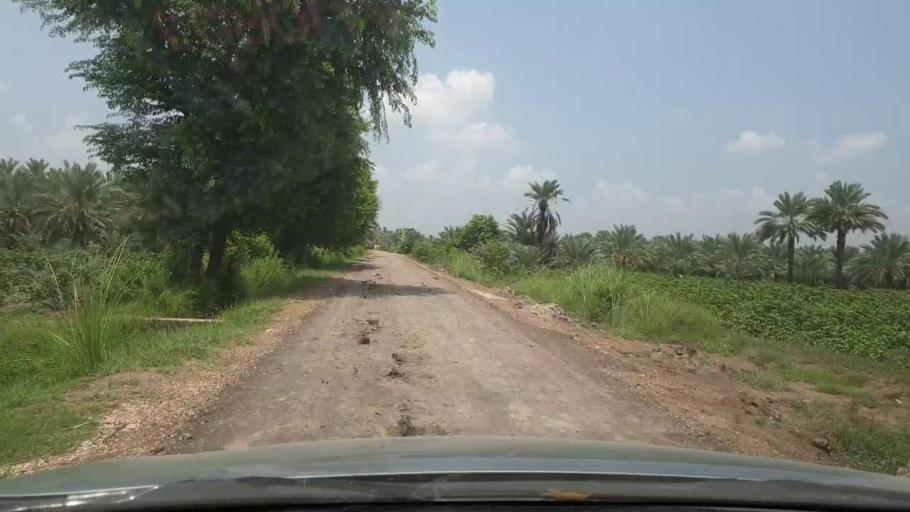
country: PK
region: Sindh
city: Khairpur
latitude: 27.4689
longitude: 68.7358
